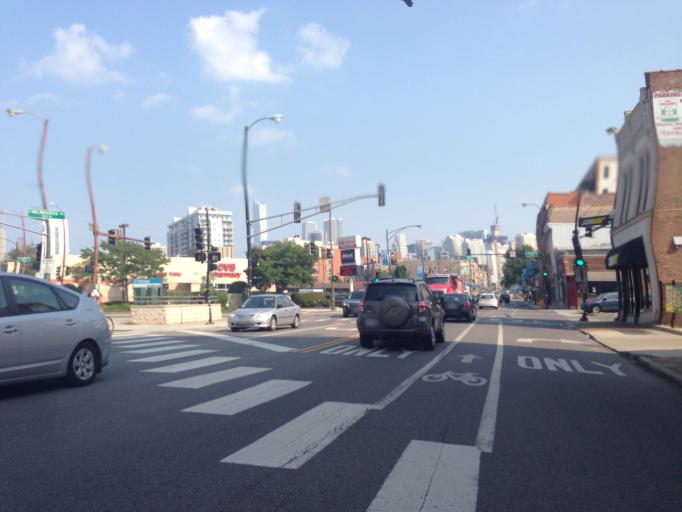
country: US
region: Illinois
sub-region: Cook County
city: Chicago
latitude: 41.8963
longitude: -87.6555
